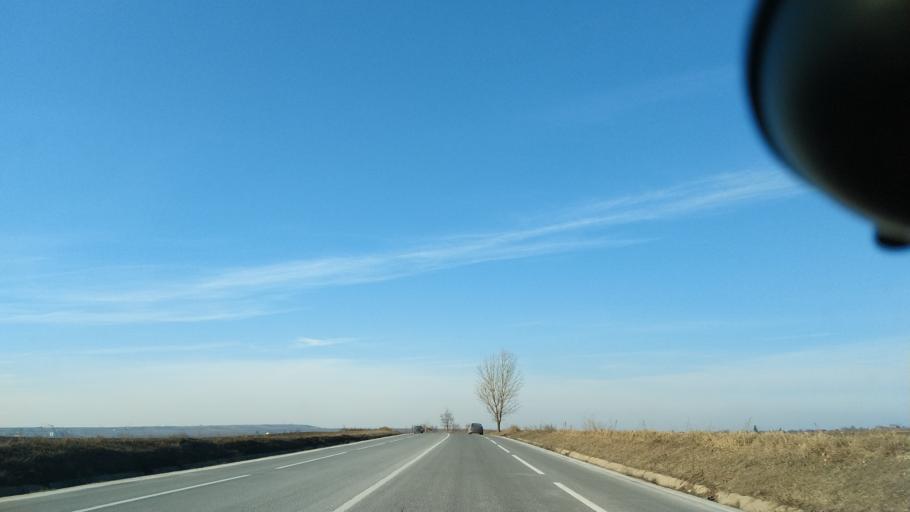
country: RO
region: Iasi
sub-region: Comuna Podu Iloaiei
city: Budai
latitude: 47.2233
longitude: 27.1945
